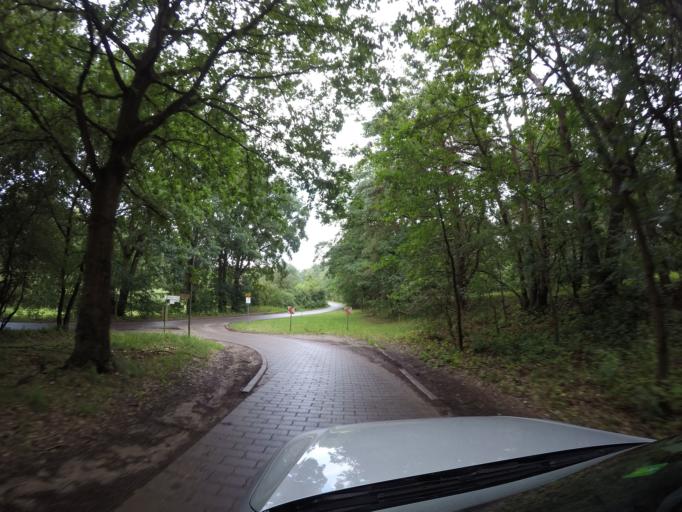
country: DE
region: Mecklenburg-Vorpommern
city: Mollenhagen
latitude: 53.4058
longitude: 12.9072
